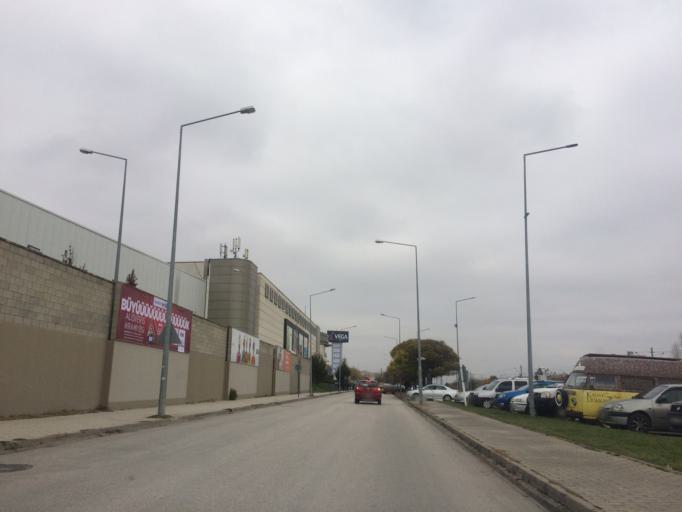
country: TR
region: Eskisehir
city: Eskisehir
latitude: 39.7795
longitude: 30.4772
